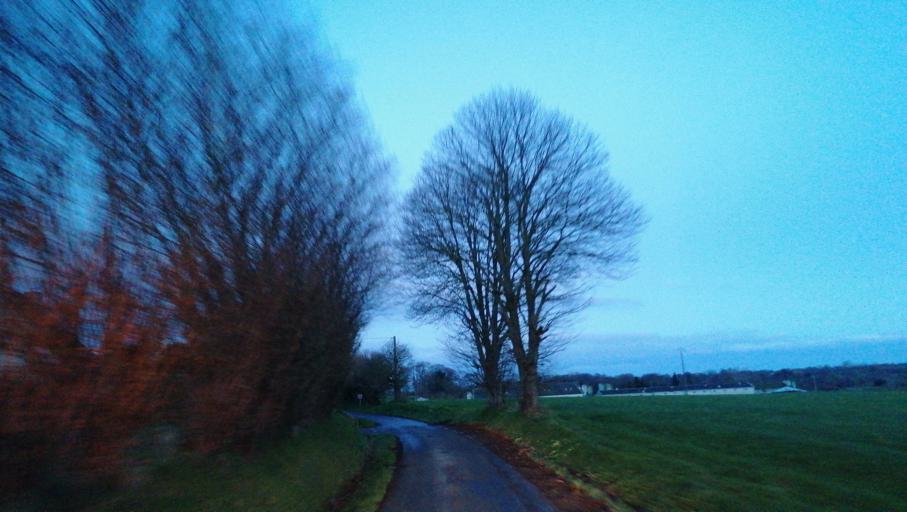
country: FR
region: Brittany
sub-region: Departement des Cotes-d'Armor
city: Plelo
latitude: 48.5550
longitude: -2.9518
